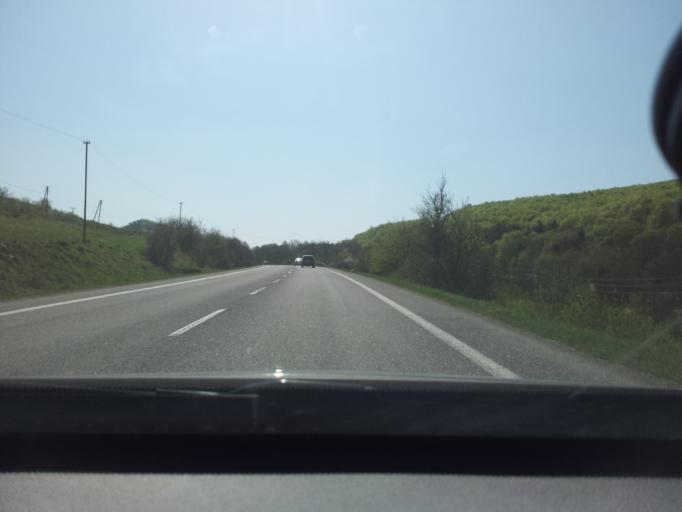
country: SK
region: Trenciansky
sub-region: Okres Trencin
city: Trencin
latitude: 48.8191
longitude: 18.0785
